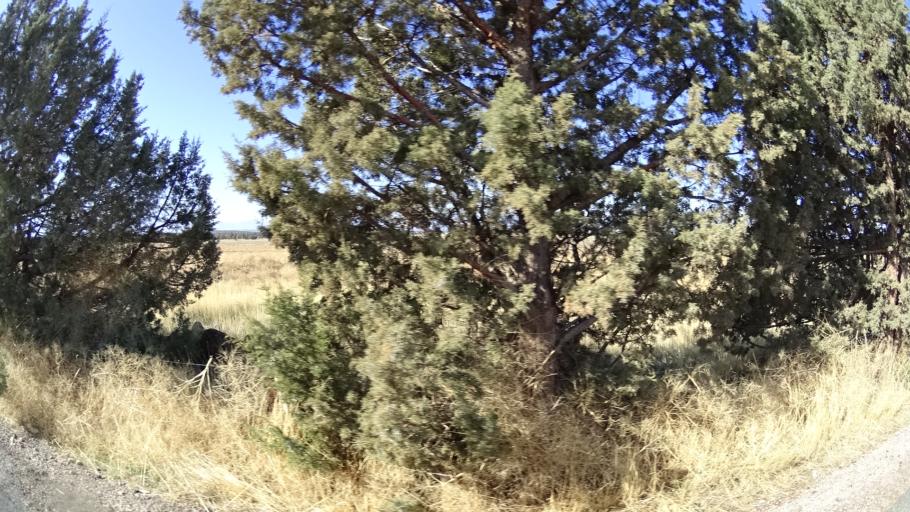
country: US
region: California
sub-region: Siskiyou County
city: Weed
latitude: 41.5970
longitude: -122.3019
